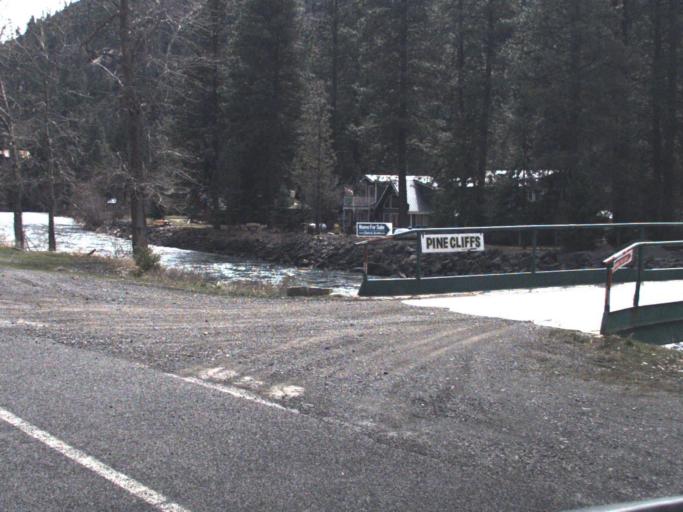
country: US
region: Washington
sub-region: Kittitas County
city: Cle Elum
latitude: 46.9003
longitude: -121.0118
